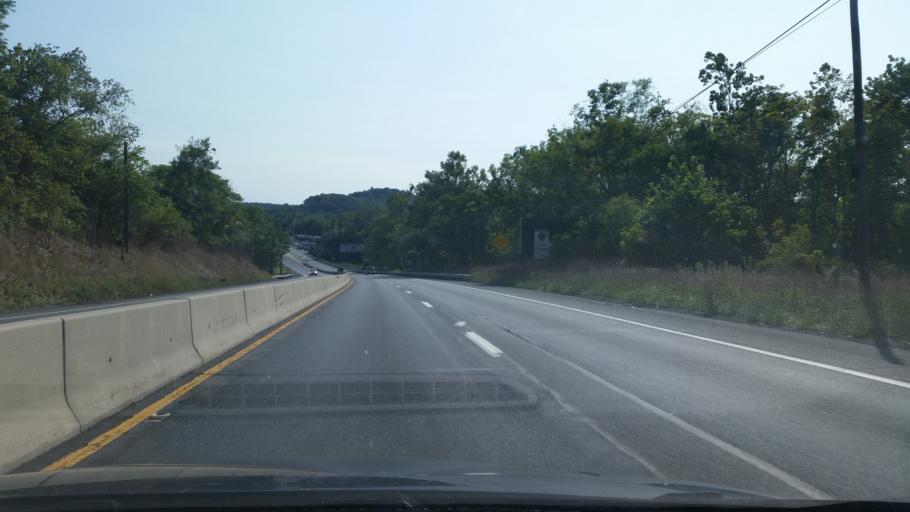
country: US
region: Pennsylvania
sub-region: Berks County
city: Leesport
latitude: 40.4674
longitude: -75.9708
